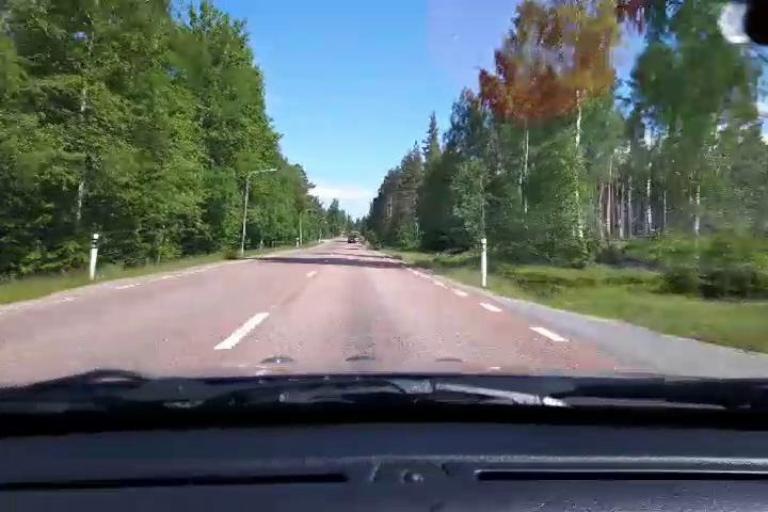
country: SE
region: Gaevleborg
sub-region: Hudiksvalls Kommun
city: Delsbo
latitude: 61.8016
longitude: 16.4823
